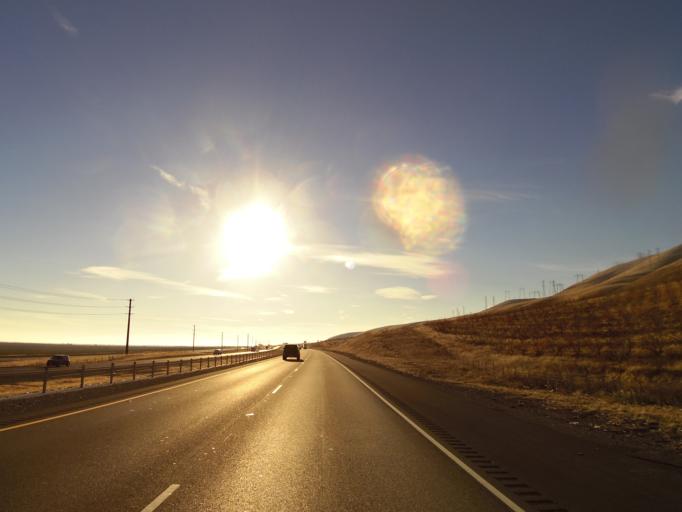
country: US
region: California
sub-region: Stanislaus County
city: Patterson
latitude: 37.5056
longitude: -121.2266
